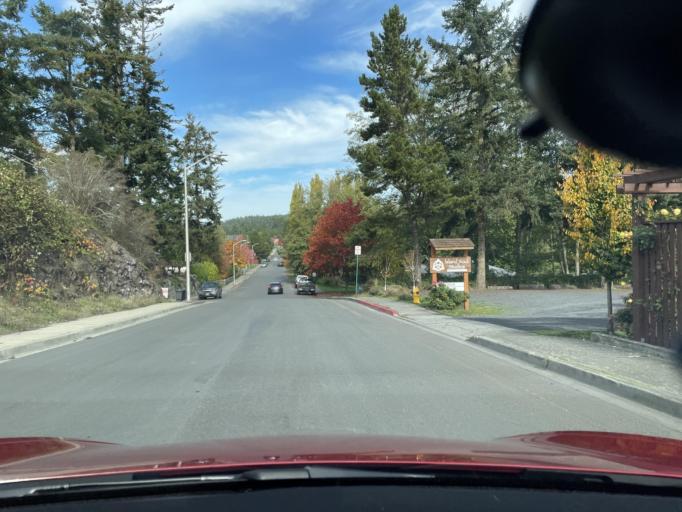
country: US
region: Washington
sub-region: San Juan County
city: Friday Harbor
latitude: 48.5372
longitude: -123.0285
